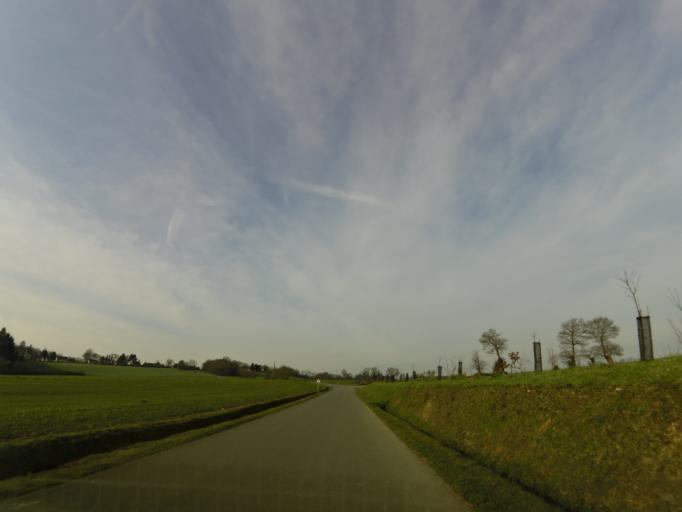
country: FR
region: Brittany
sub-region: Departement d'Ille-et-Vilaine
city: Pance
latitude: 47.8861
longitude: -1.6514
